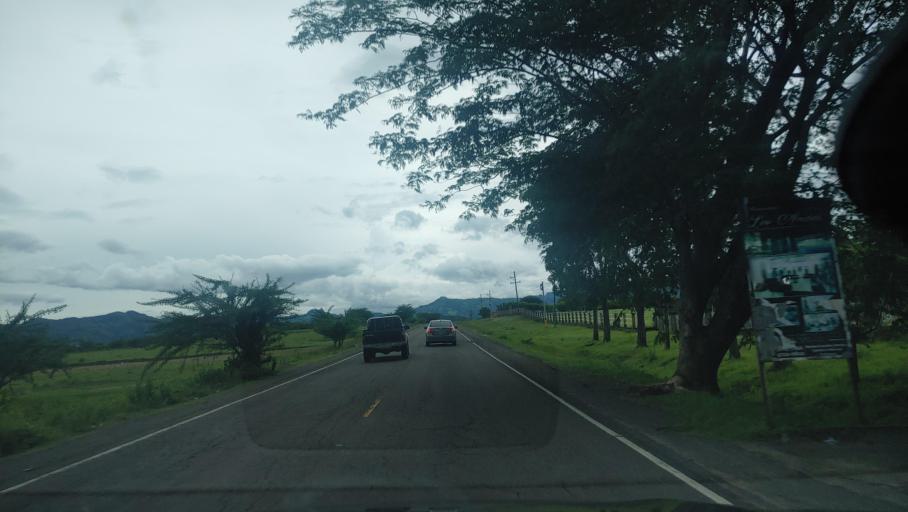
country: HN
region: Choluteca
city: Santa Ana de Yusguare
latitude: 13.3425
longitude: -87.1230
